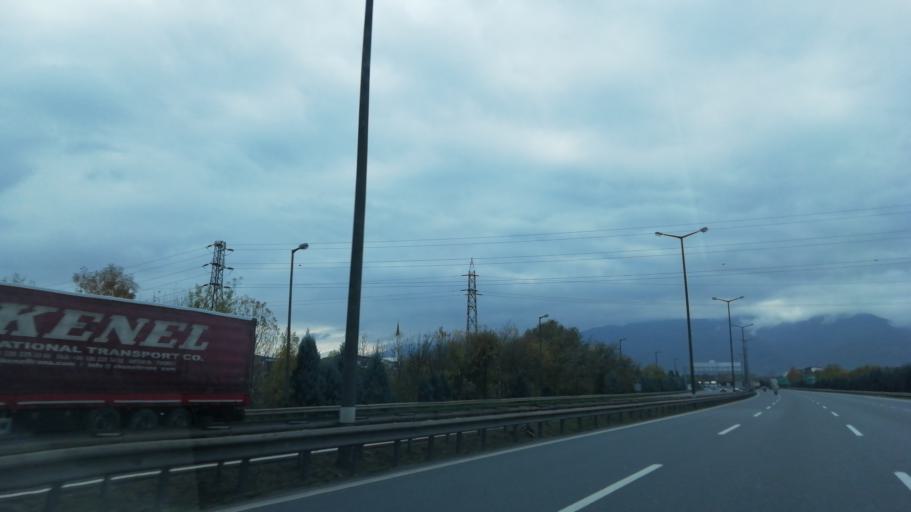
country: TR
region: Kocaeli
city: Kosekoy
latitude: 40.7449
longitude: 30.0423
